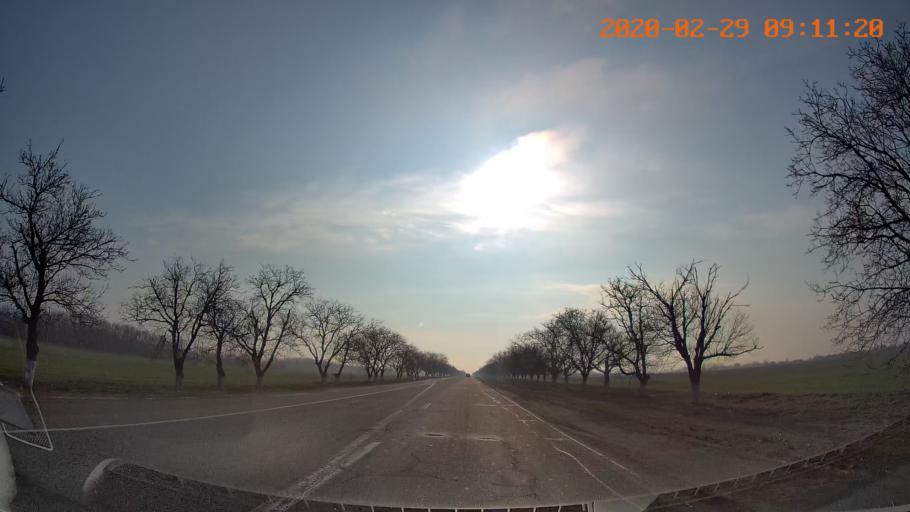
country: MD
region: Telenesti
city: Slobozia
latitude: 46.8361
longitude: 29.7978
